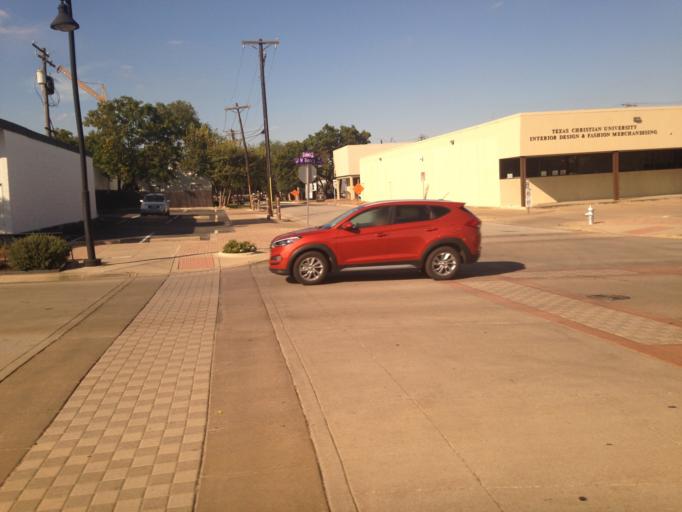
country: US
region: Texas
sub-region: Tarrant County
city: Fort Worth
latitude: 32.7061
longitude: -97.3569
